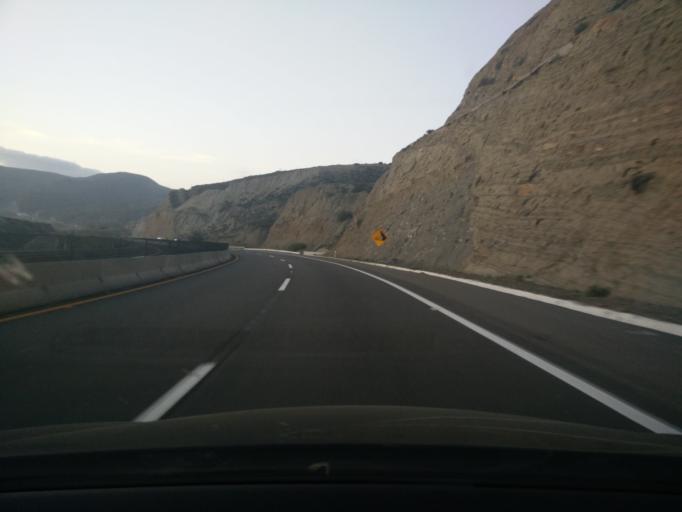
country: MX
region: Baja California
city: El Sauzal
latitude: 31.9562
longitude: -116.7569
